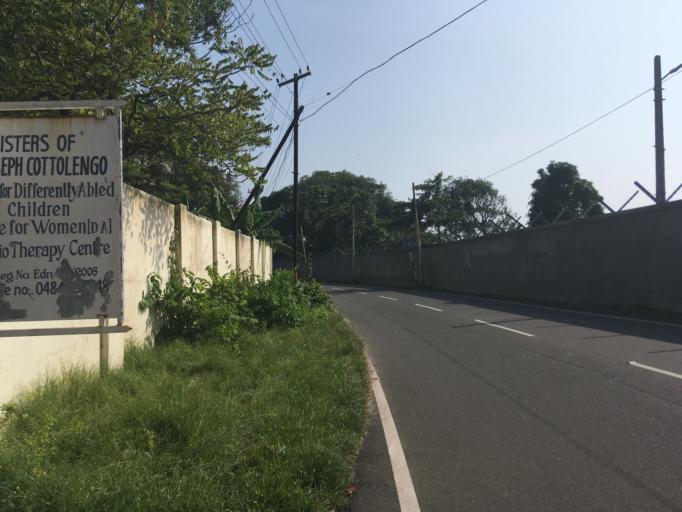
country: IN
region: Kerala
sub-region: Ernakulam
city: Cochin
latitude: 9.9623
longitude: 76.2376
